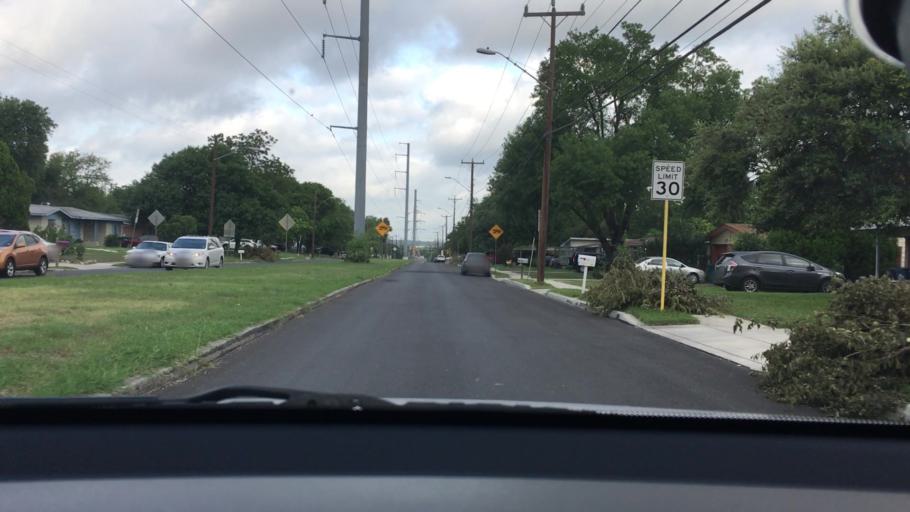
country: US
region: Texas
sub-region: Bexar County
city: Windcrest
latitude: 29.5033
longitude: -98.4029
